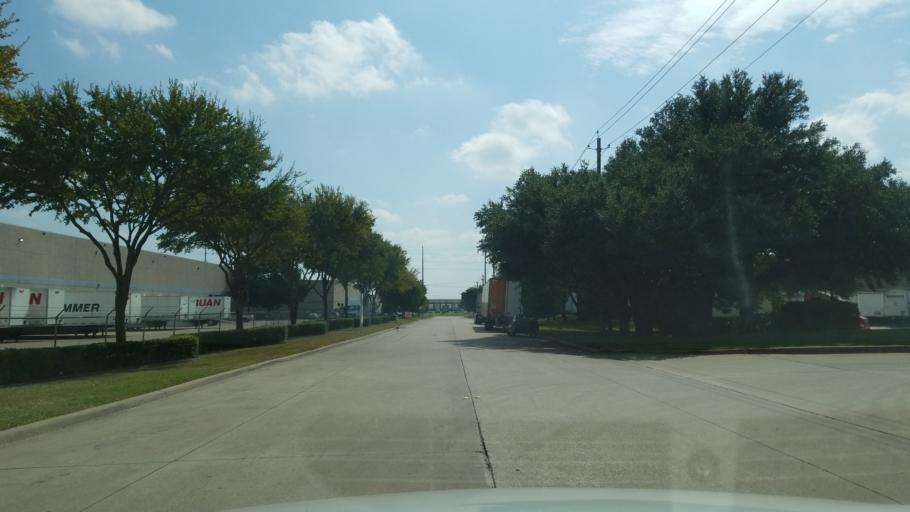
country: US
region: Texas
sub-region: Dallas County
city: Garland
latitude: 32.9037
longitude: -96.6711
